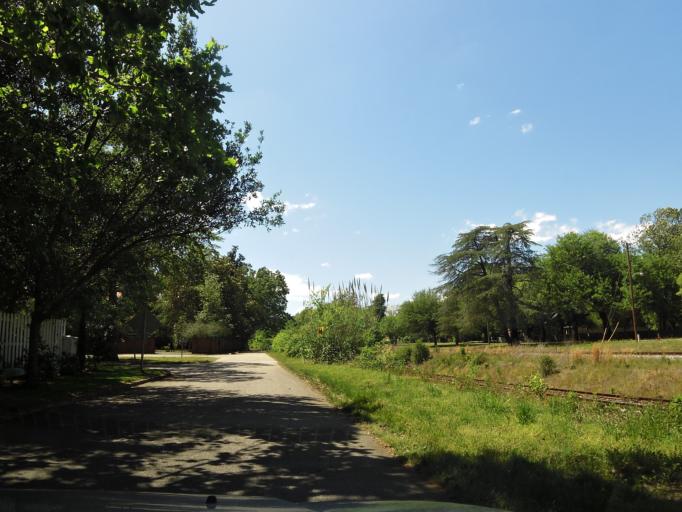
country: US
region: South Carolina
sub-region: Aiken County
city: Aiken
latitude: 33.5556
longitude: -81.7116
